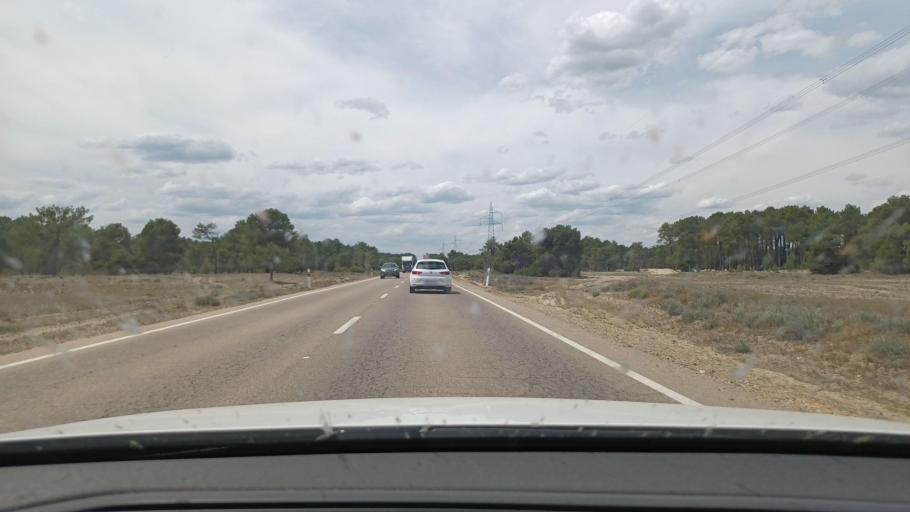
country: ES
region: Castille and Leon
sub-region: Provincia de Segovia
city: Cantalejo
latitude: 41.2921
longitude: -4.0056
